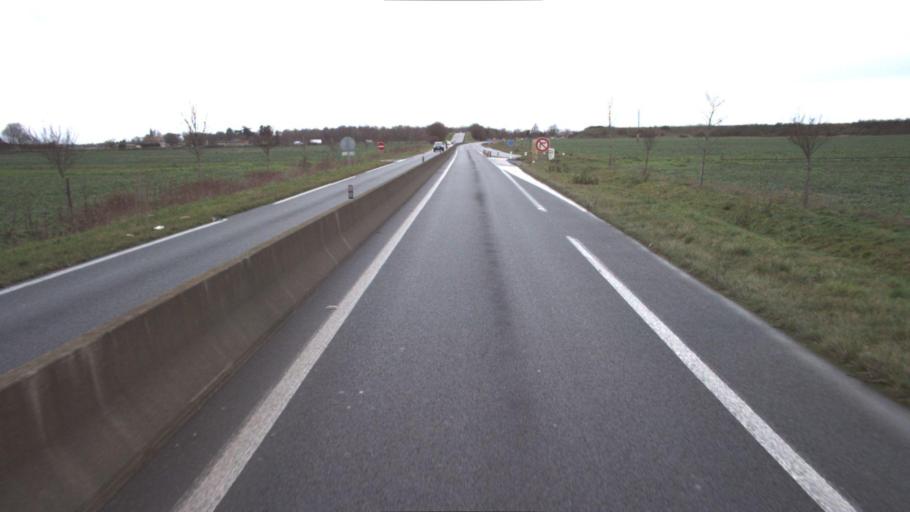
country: FR
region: Ile-de-France
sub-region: Departement de l'Essonne
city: Le Coudray-Montceaux
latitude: 48.5558
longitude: 2.4990
